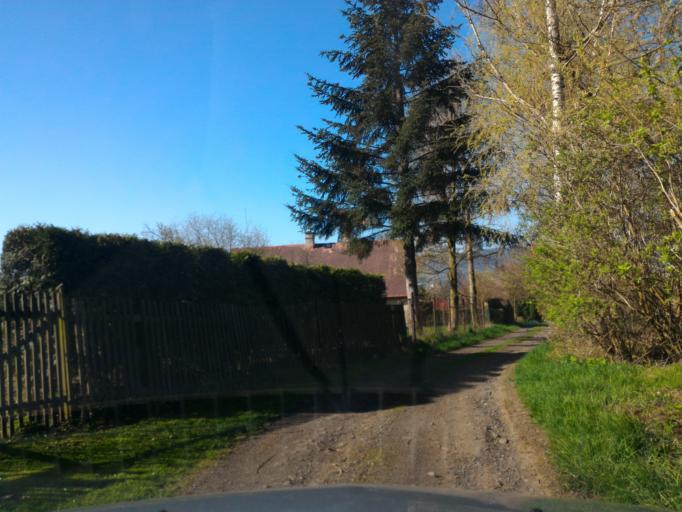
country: CZ
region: Ustecky
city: Varnsdorf
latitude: 50.9236
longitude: 14.6342
